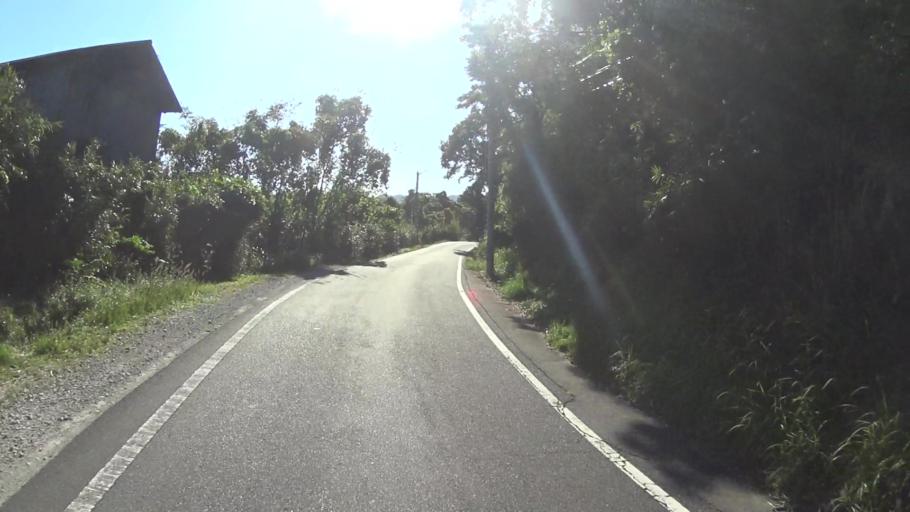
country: JP
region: Hyogo
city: Toyooka
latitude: 35.6387
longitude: 134.8947
